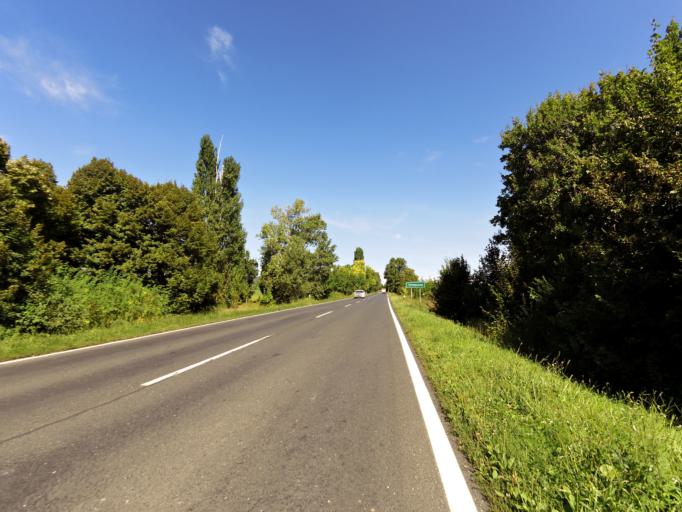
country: HU
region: Veszprem
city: Tapolca
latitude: 46.8301
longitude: 17.3775
